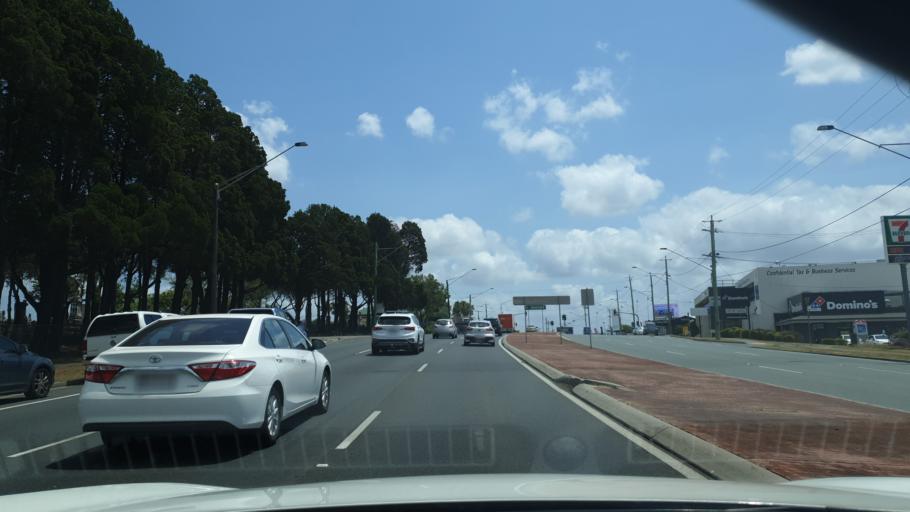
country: AU
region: Queensland
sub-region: Brisbane
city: Wavell Heights
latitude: -27.4015
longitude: 153.0314
